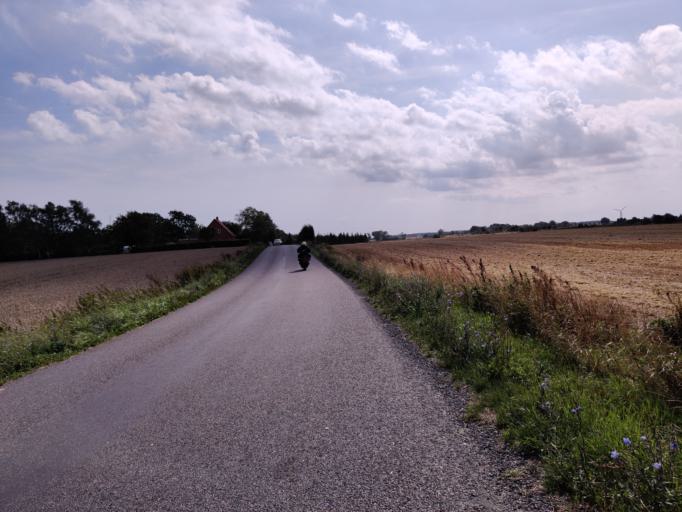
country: DK
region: Zealand
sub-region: Guldborgsund Kommune
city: Nykobing Falster
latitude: 54.6753
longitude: 11.9004
